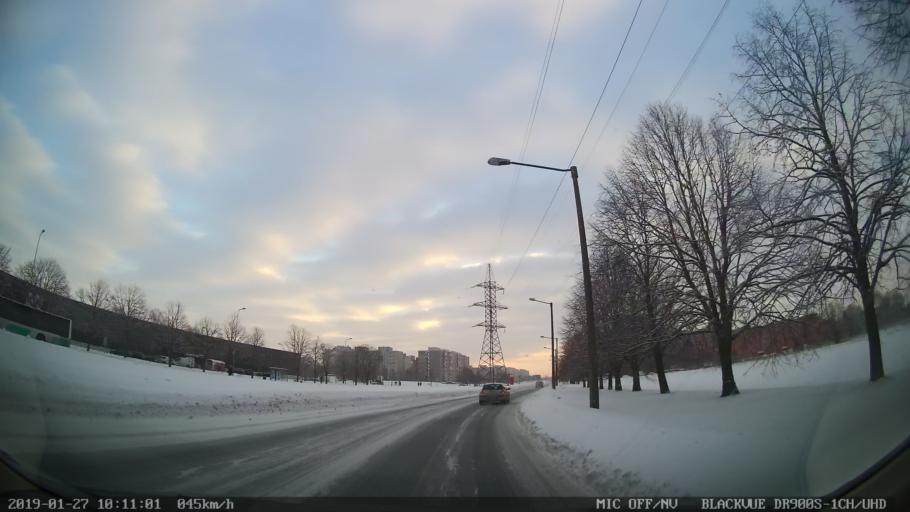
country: EE
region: Harju
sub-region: Viimsi vald
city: Viimsi
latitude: 59.4436
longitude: 24.8211
